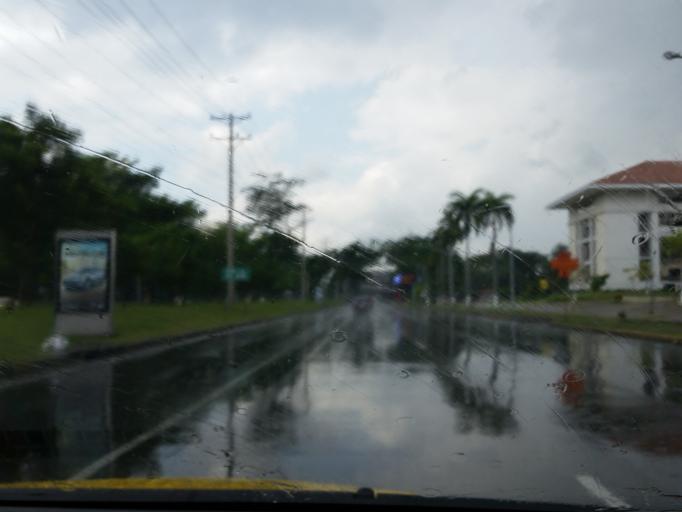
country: PA
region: Panama
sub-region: Distrito de Panama
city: Ancon
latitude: 8.9661
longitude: -79.5473
